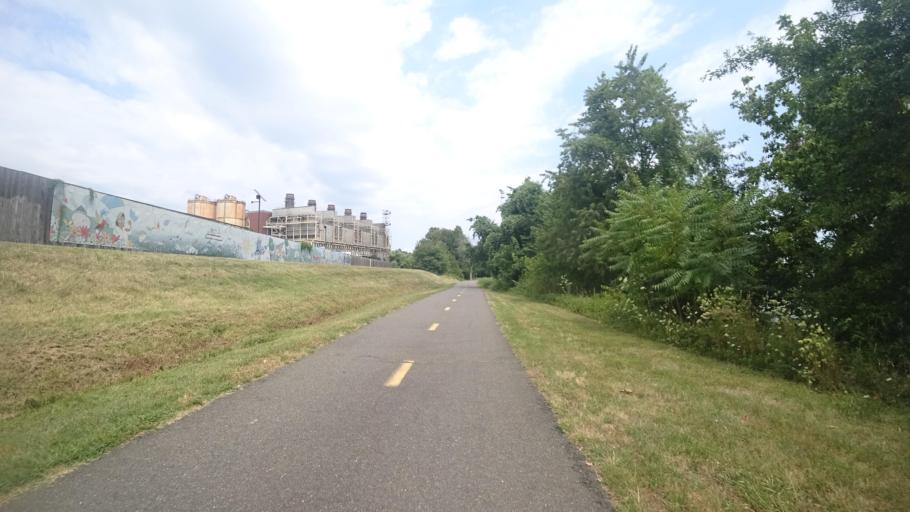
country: US
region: Virginia
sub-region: City of Alexandria
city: Alexandria
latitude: 38.8182
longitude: -77.0391
